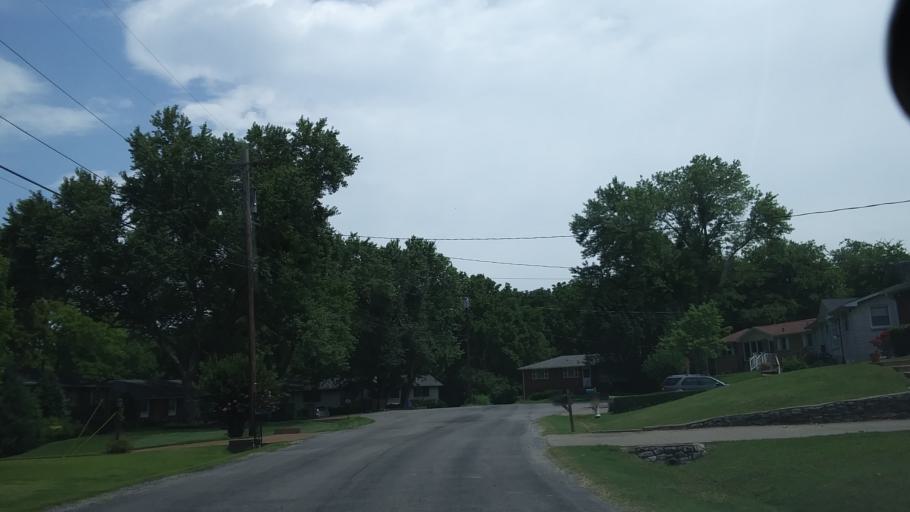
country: US
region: Tennessee
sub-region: Davidson County
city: Belle Meade
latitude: 36.1493
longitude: -86.8880
